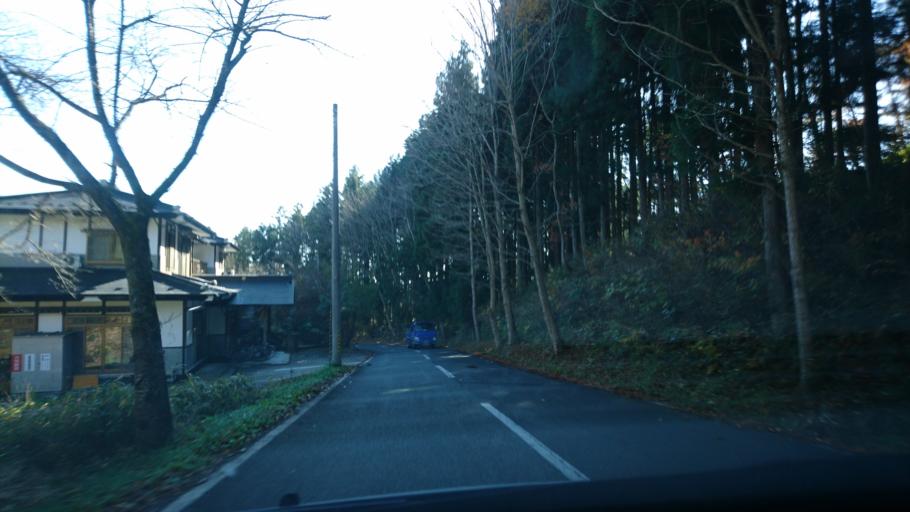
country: JP
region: Iwate
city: Ichinoseki
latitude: 38.9907
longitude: 141.1083
